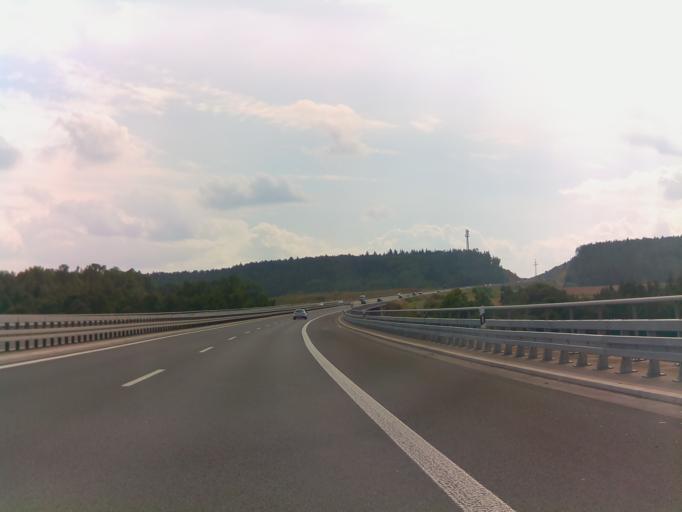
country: DE
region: Bavaria
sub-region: Regierungsbezirk Unterfranken
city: Hollstadt
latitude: 50.3438
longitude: 10.3114
